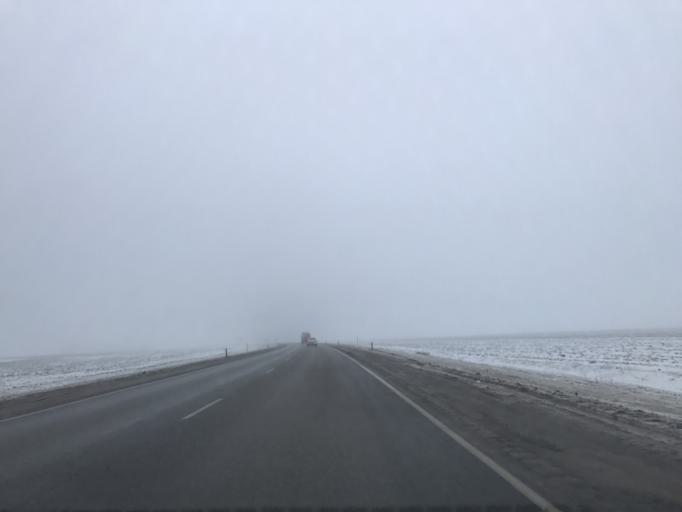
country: RU
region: Rostov
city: Temernik
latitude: 47.3651
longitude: 39.7119
